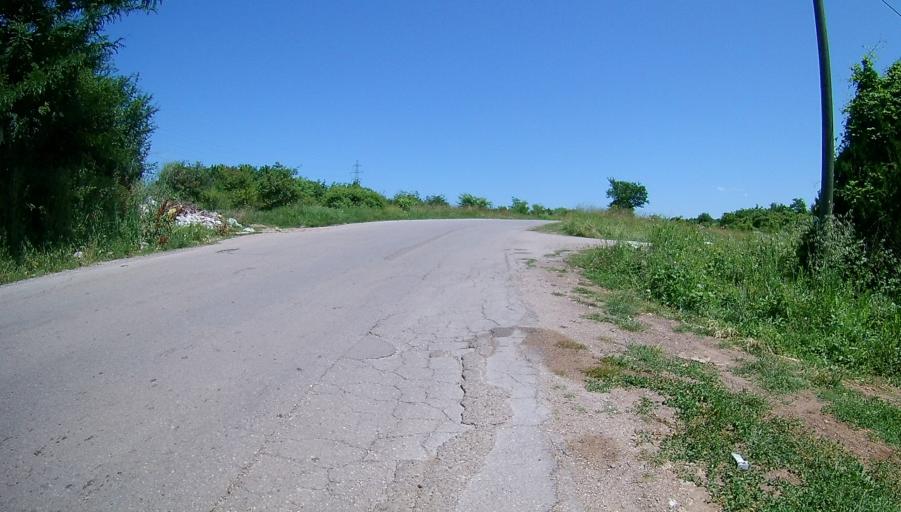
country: RS
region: Central Serbia
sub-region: Nisavski Okrug
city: Nis
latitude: 43.2957
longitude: 21.8888
